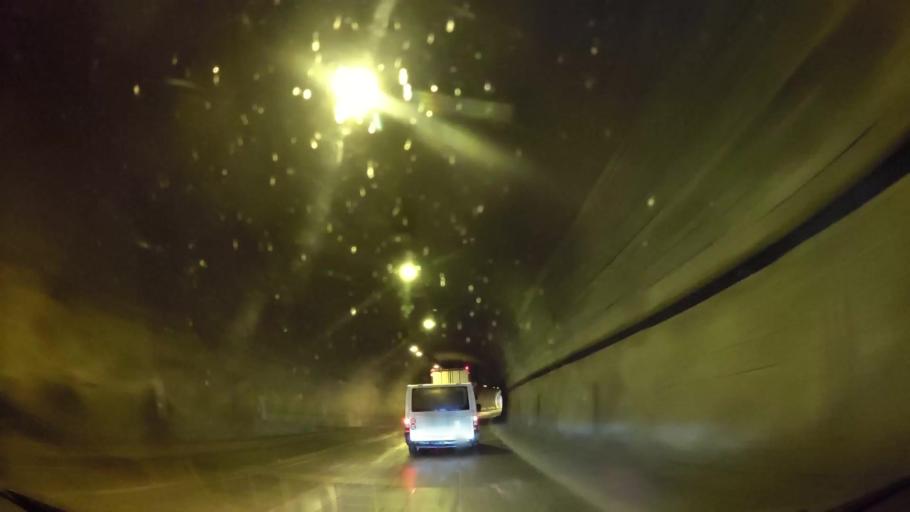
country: RS
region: Central Serbia
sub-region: Pcinjski Okrug
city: Vladicin Han
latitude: 42.7258
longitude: 22.0675
